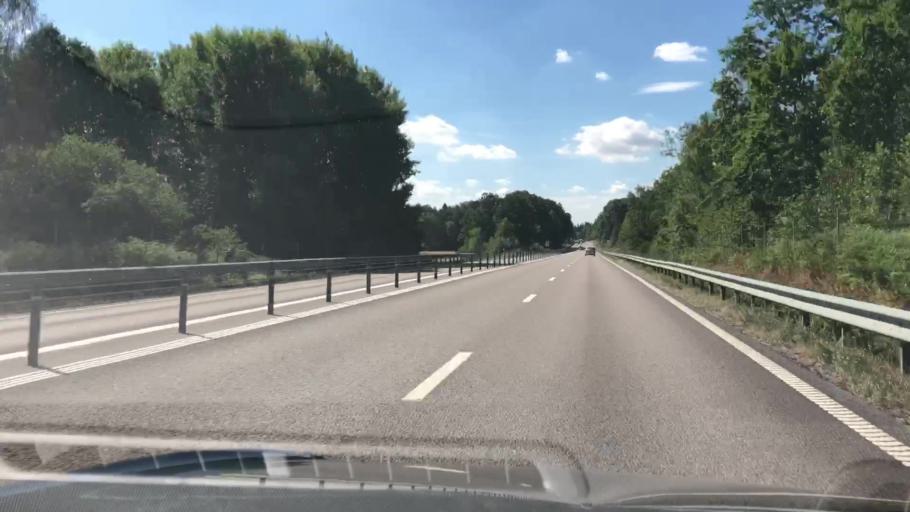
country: SE
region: Kalmar
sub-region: Monsteras Kommun
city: Timmernabben
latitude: 56.9125
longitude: 16.3830
